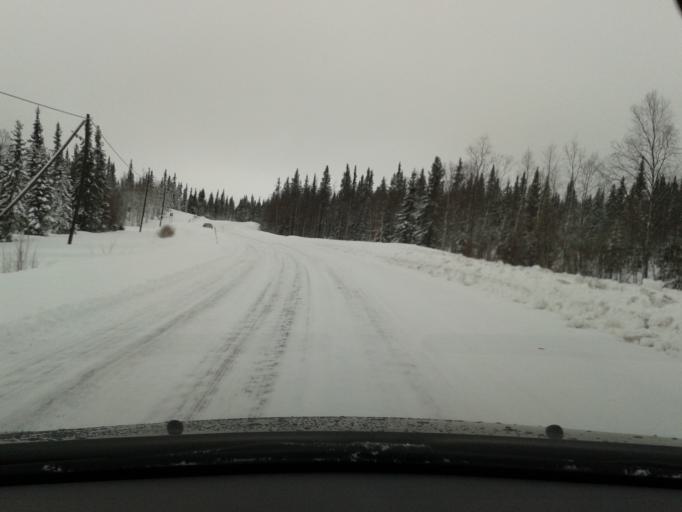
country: SE
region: Vaesterbotten
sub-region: Vilhelmina Kommun
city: Sjoberg
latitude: 65.1831
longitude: 15.8901
